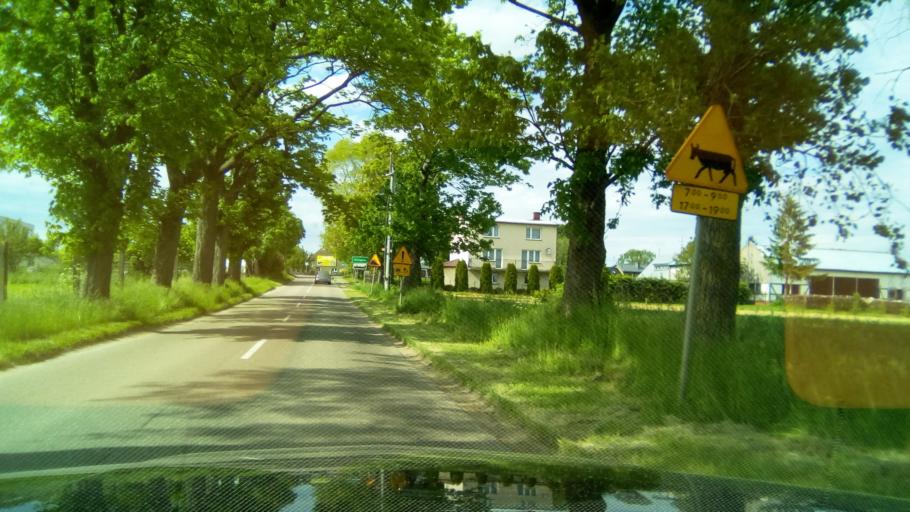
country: PL
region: Pomeranian Voivodeship
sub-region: Powiat pucki
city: Krokowa
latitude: 54.7920
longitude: 18.1173
